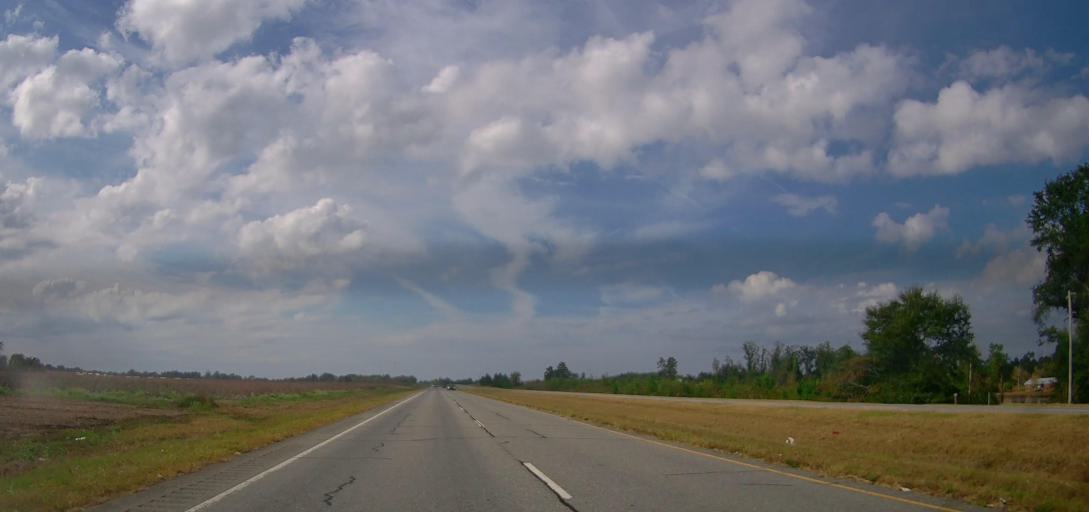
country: US
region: Georgia
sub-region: Mitchell County
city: Pelham
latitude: 31.1082
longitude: -84.1171
